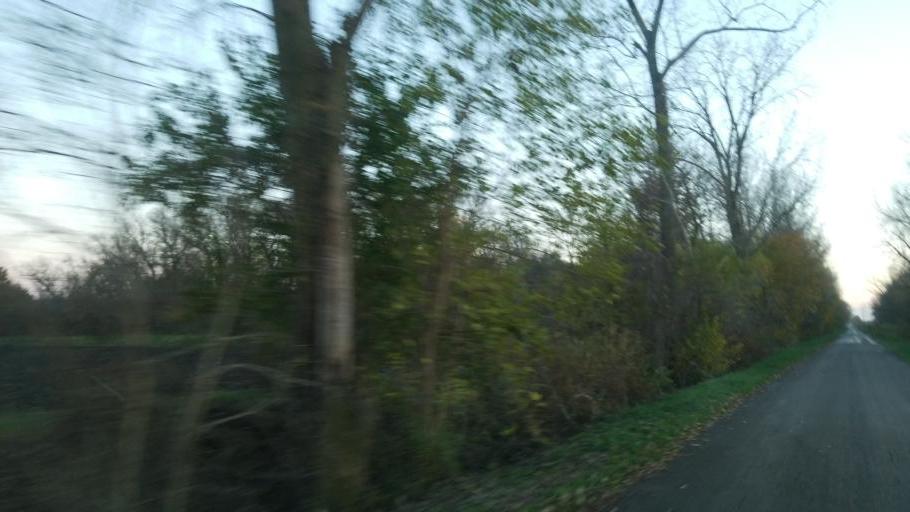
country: US
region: Ohio
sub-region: Huron County
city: Willard
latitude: 41.0220
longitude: -82.7813
